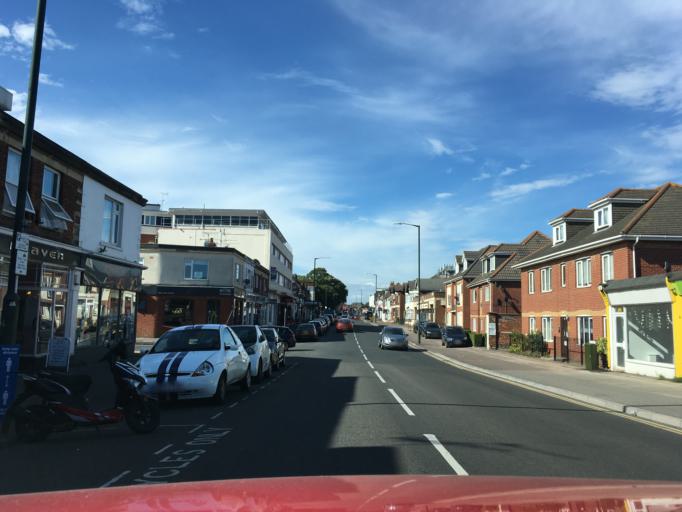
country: GB
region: England
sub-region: Bournemouth
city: Bournemouth
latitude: 50.7474
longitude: -1.8778
